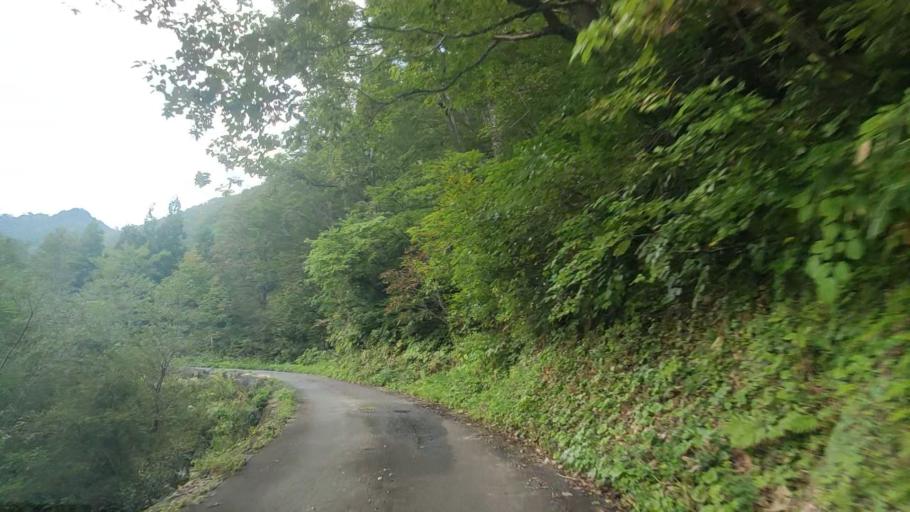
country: JP
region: Toyama
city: Yatsuomachi-higashikumisaka
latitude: 36.3367
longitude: 137.0755
